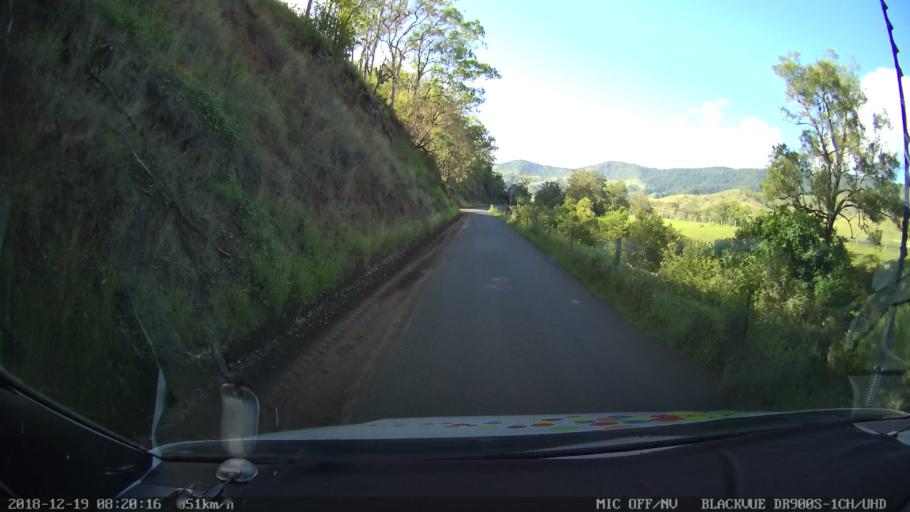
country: AU
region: New South Wales
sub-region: Kyogle
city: Kyogle
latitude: -28.2890
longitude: 152.9100
